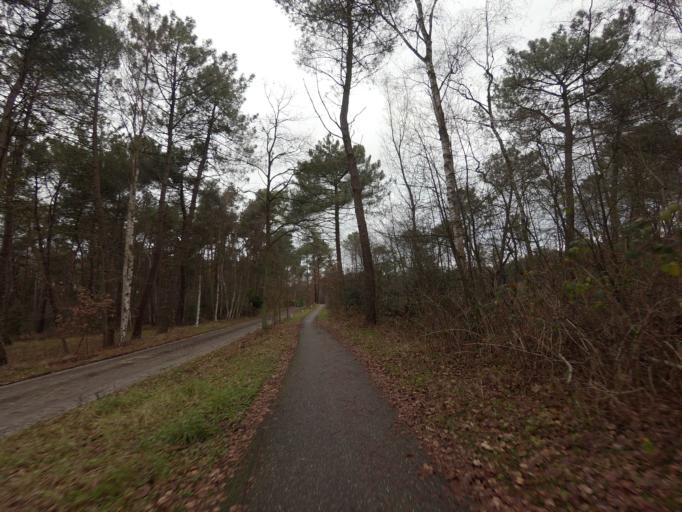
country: BE
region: Flanders
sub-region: Provincie Antwerpen
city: Stabroek
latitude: 51.3699
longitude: 4.3372
